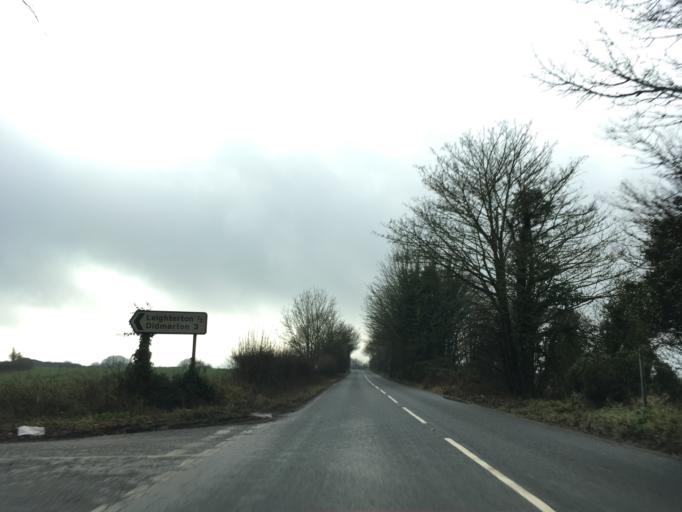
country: GB
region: England
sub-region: Gloucestershire
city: Nailsworth
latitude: 51.6289
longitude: -2.2576
